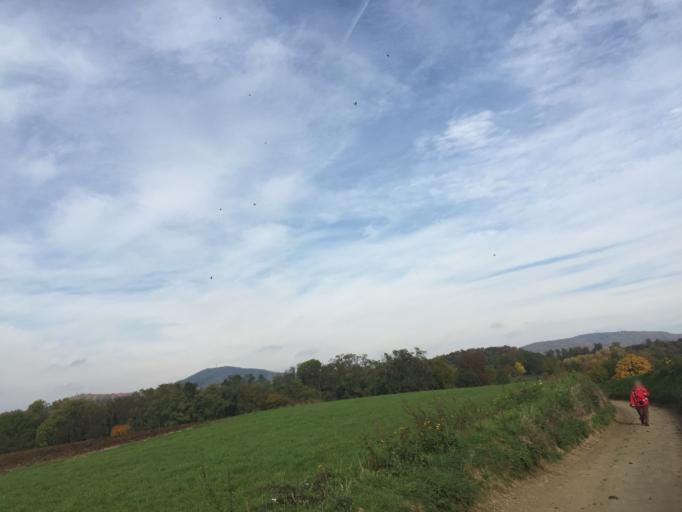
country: DE
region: Hesse
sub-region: Regierungsbezirk Darmstadt
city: Bensheim
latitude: 49.6811
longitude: 8.6492
